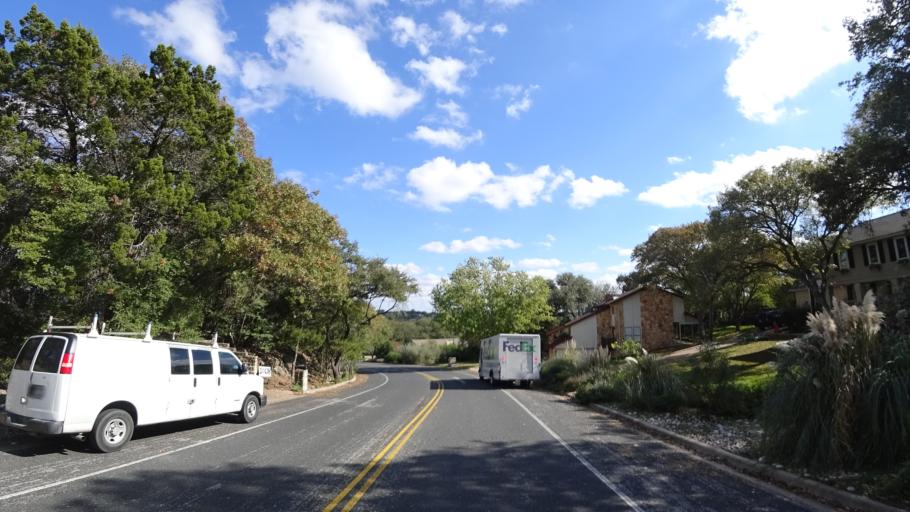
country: US
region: Texas
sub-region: Williamson County
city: Anderson Mill
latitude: 30.4307
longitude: -97.8035
